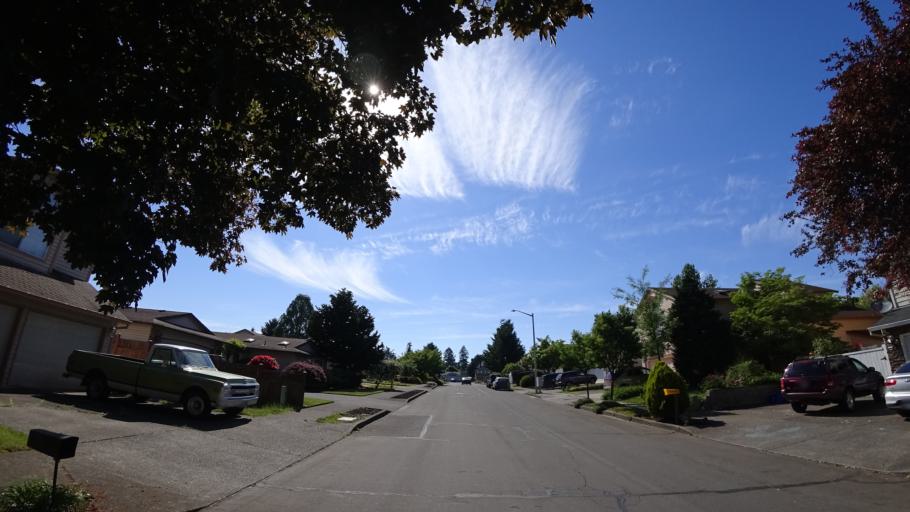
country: US
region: Oregon
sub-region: Multnomah County
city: Gresham
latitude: 45.4920
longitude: -122.4698
